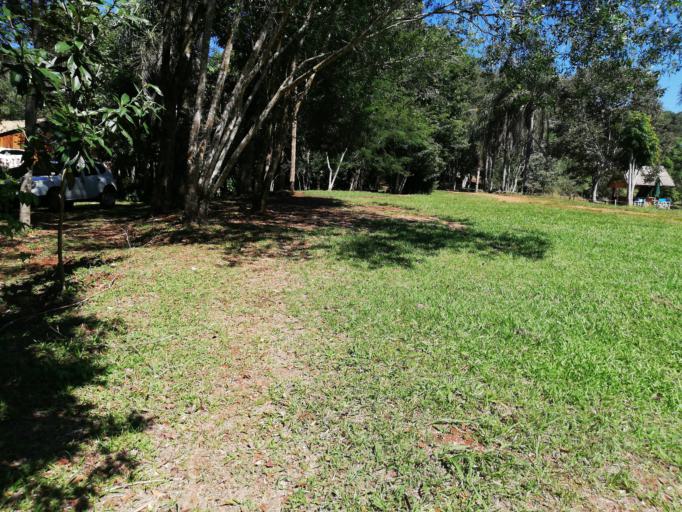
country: AR
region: Misiones
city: Dos de Mayo
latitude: -27.0459
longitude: -54.4000
